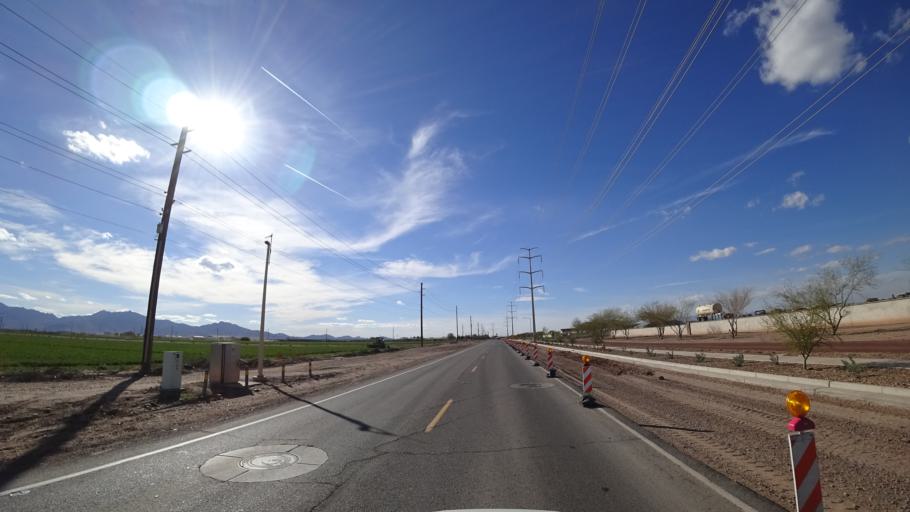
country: US
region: Arizona
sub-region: Maricopa County
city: Tolleson
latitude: 33.4085
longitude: -112.2322
